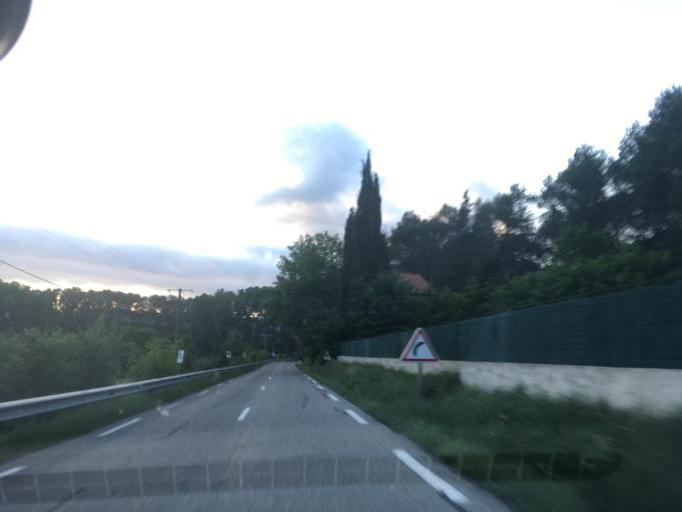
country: FR
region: Provence-Alpes-Cote d'Azur
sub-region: Departement du Var
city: Salernes
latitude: 43.5451
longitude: 6.2523
